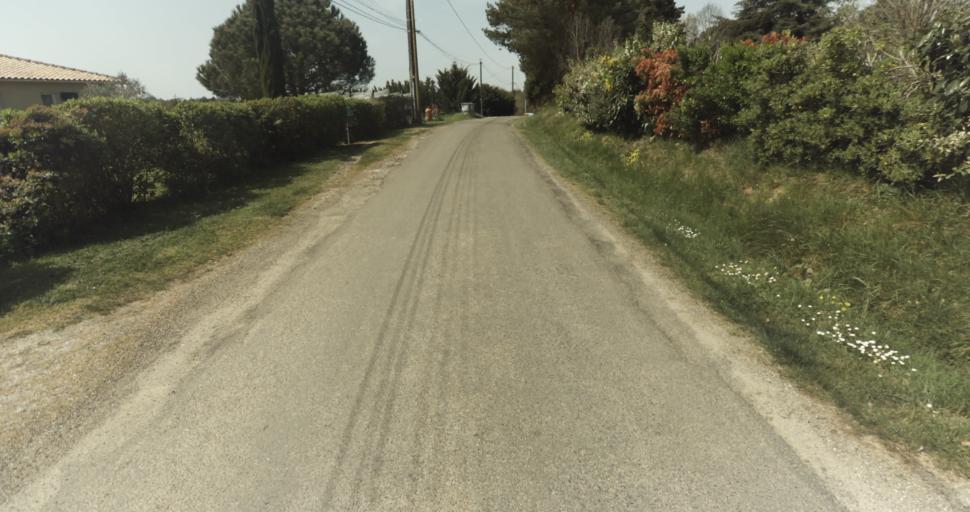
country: FR
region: Midi-Pyrenees
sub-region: Departement du Tarn-et-Garonne
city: Moissac
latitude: 44.1295
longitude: 1.0823
